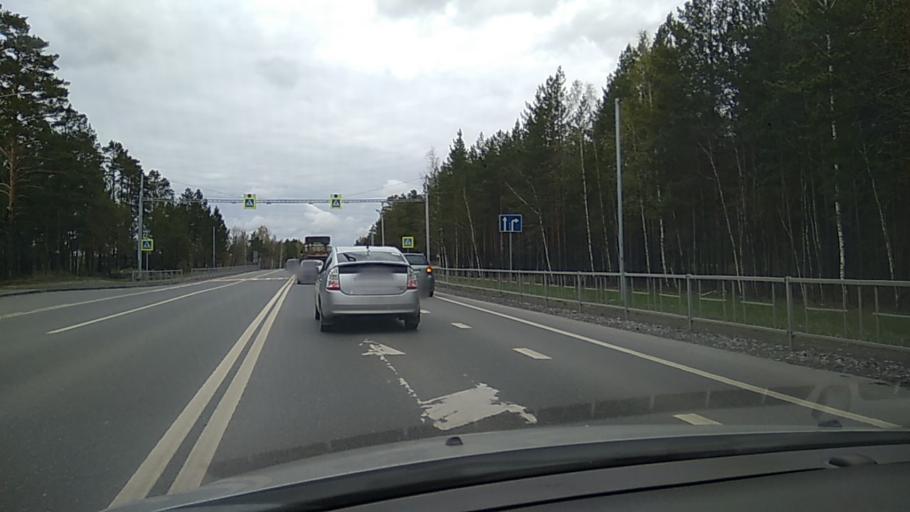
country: RU
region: Tjumen
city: Chervishevo
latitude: 56.9993
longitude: 65.4827
